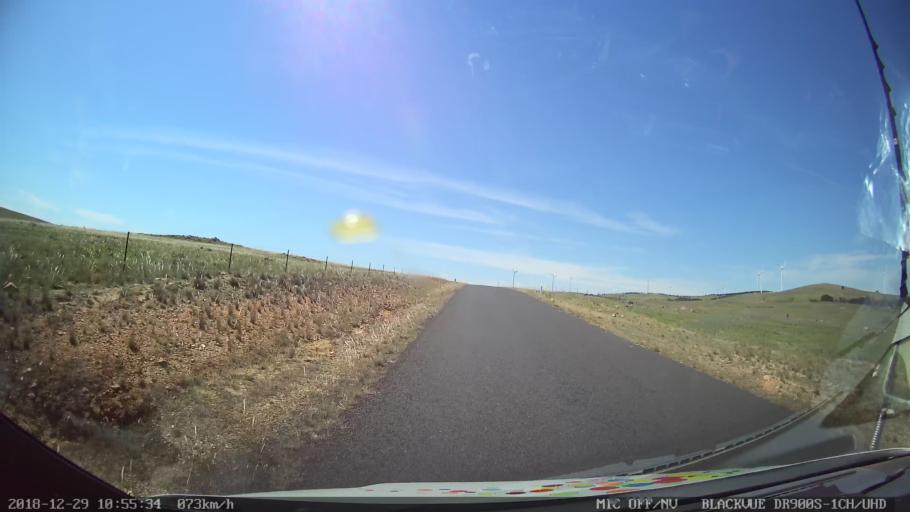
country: AU
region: New South Wales
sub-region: Palerang
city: Bungendore
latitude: -35.1266
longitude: 149.5326
